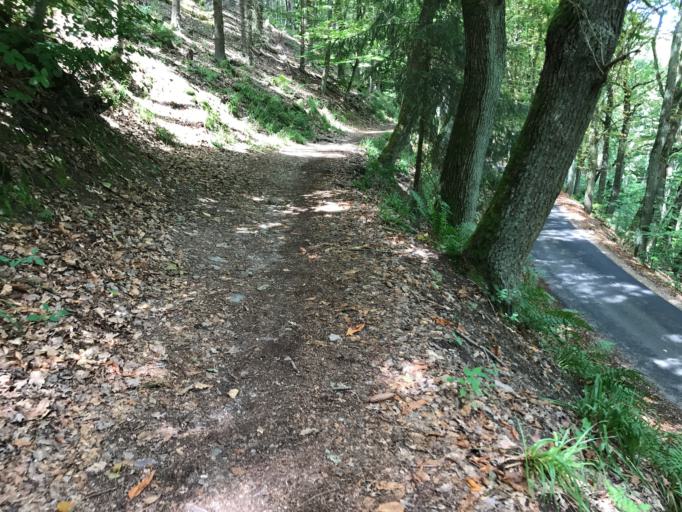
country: DE
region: Rheinland-Pfalz
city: Weiler
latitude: 49.9719
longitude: 7.8639
